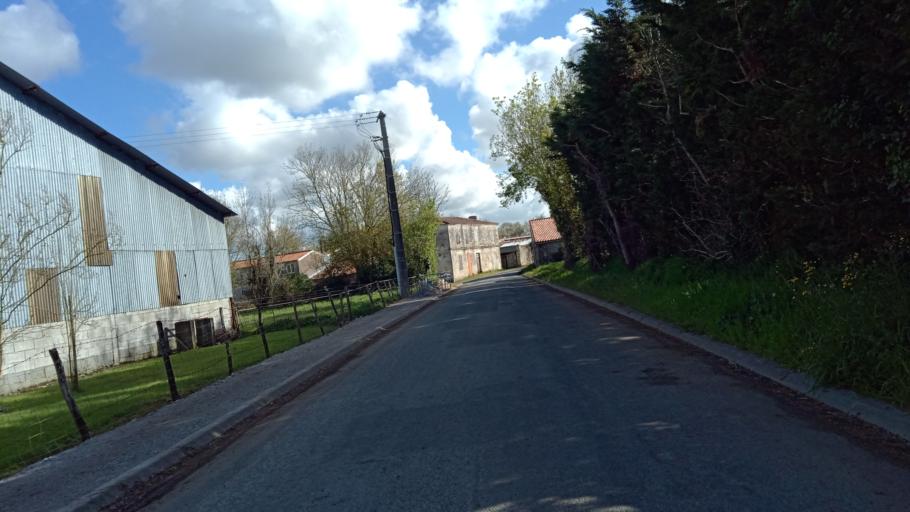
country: FR
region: Poitou-Charentes
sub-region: Departement de la Charente-Maritime
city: Verines
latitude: 46.1658
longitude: -0.9477
